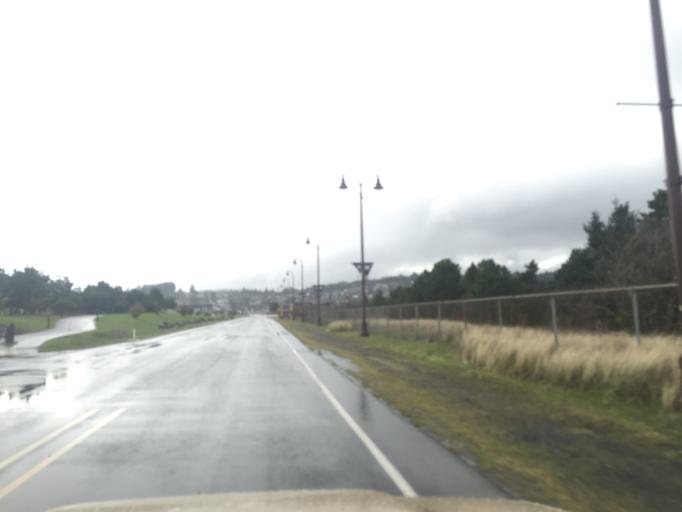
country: US
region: Oregon
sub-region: Lincoln County
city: Newport
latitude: 44.6207
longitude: -124.0476
